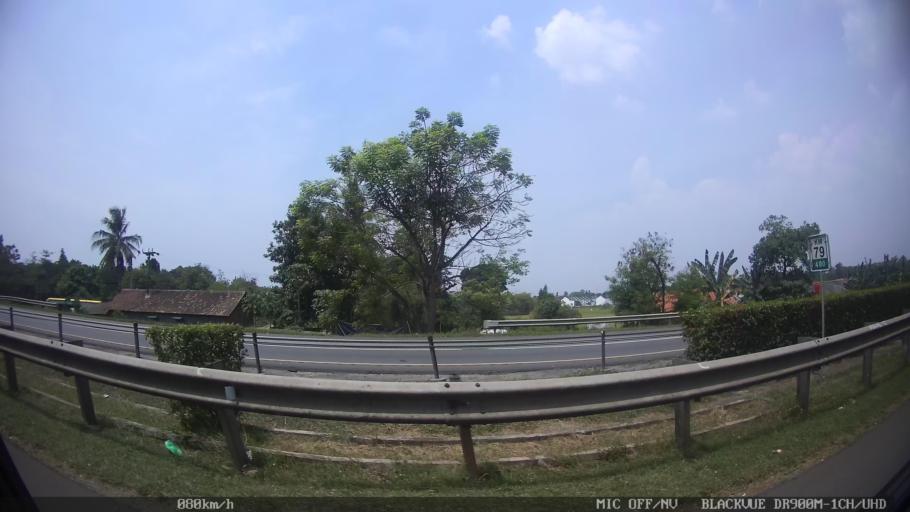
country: ID
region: Banten
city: Serang
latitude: -6.0782
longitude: 106.1321
